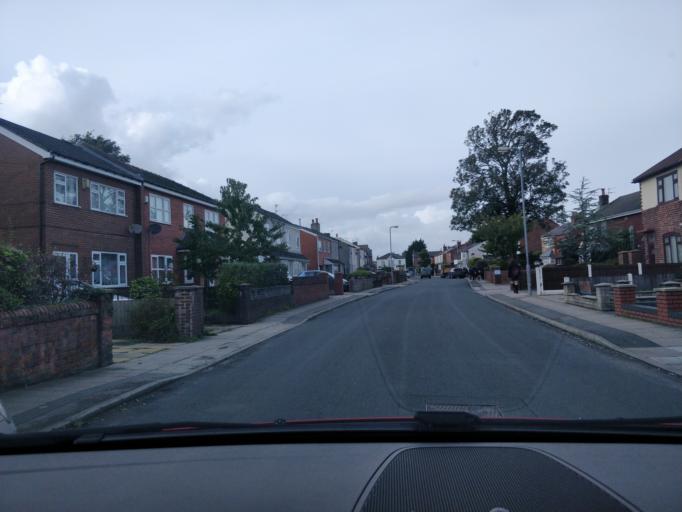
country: GB
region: England
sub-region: Sefton
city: Southport
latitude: 53.6281
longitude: -3.0052
